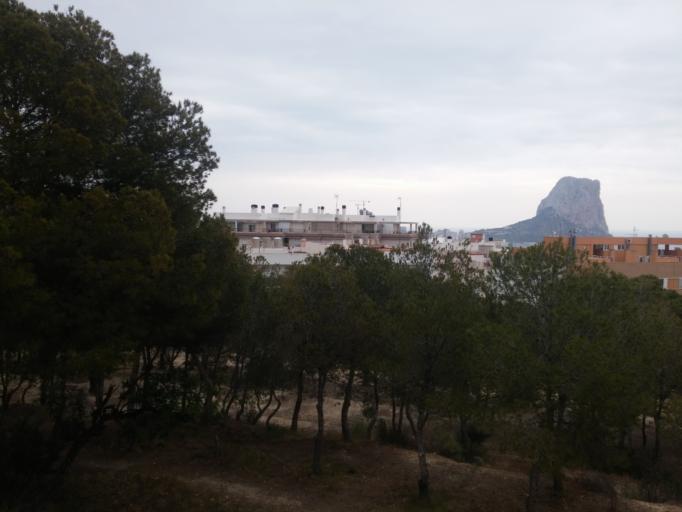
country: ES
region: Valencia
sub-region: Provincia de Alicante
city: Calp
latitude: 38.6428
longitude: 0.0411
